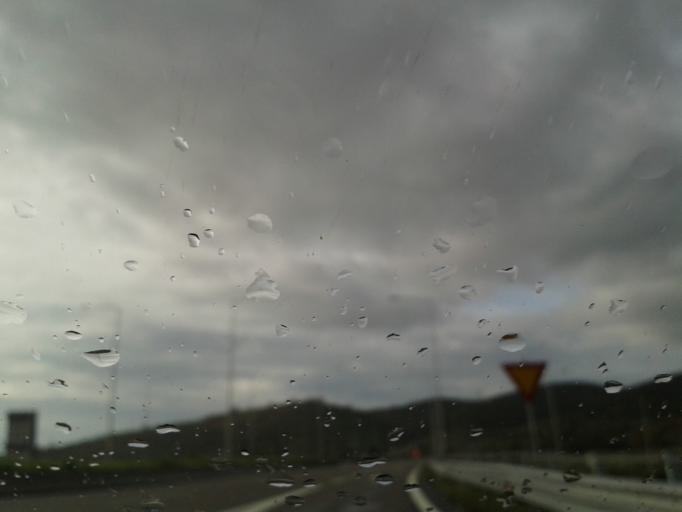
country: GR
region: West Greece
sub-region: Nomos Aitolias kai Akarnanias
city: Galatas
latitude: 38.3857
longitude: 21.5425
